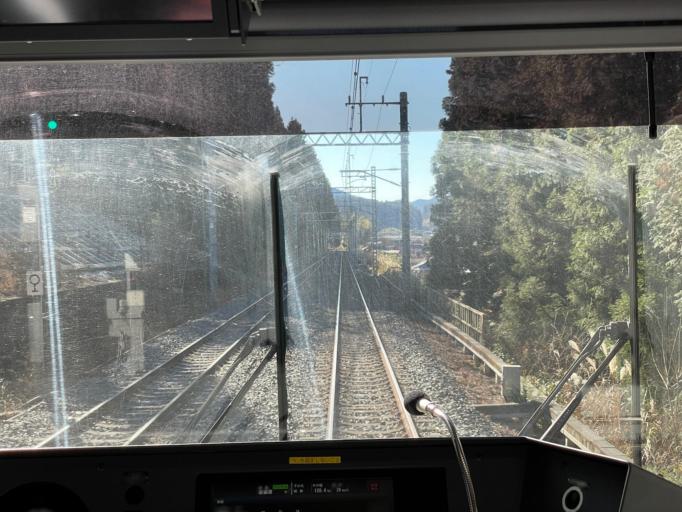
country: JP
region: Tochigi
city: Imaichi
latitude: 36.6593
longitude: 139.7139
